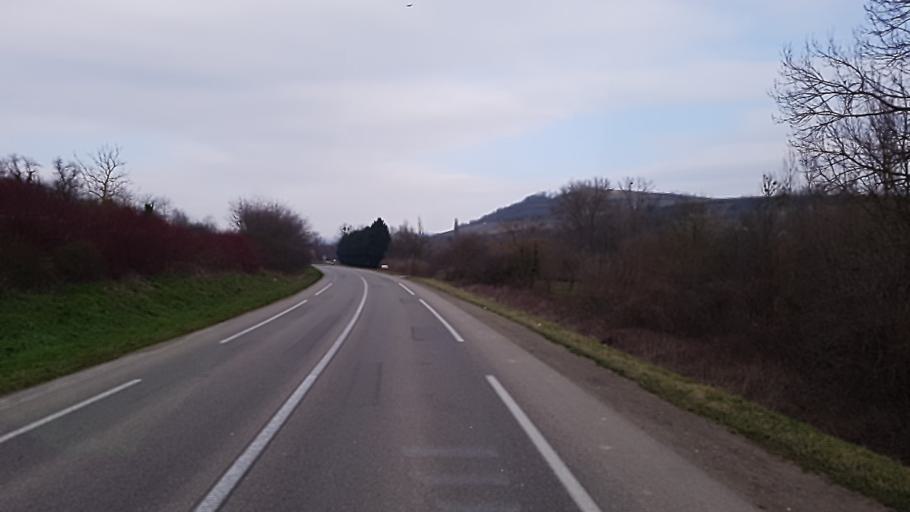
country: FR
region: Alsace
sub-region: Departement du Bas-Rhin
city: Molsheim
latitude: 48.5644
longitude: 7.4962
